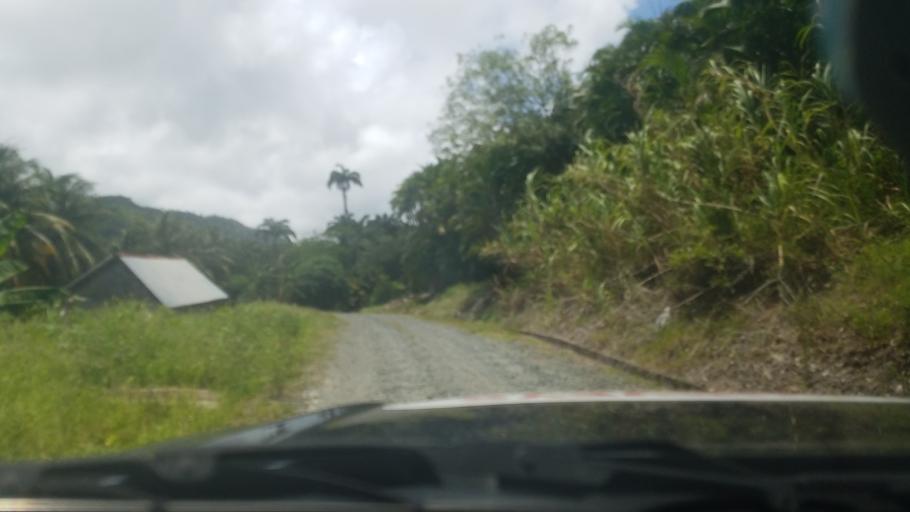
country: LC
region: Praslin
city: Praslin
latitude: 13.8674
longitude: -60.9025
